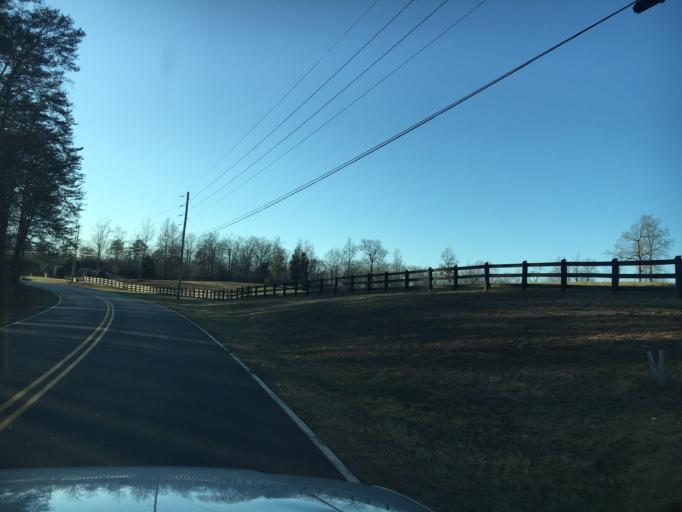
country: US
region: North Carolina
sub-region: Rutherford County
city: Rutherfordton
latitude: 35.2702
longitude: -82.0541
